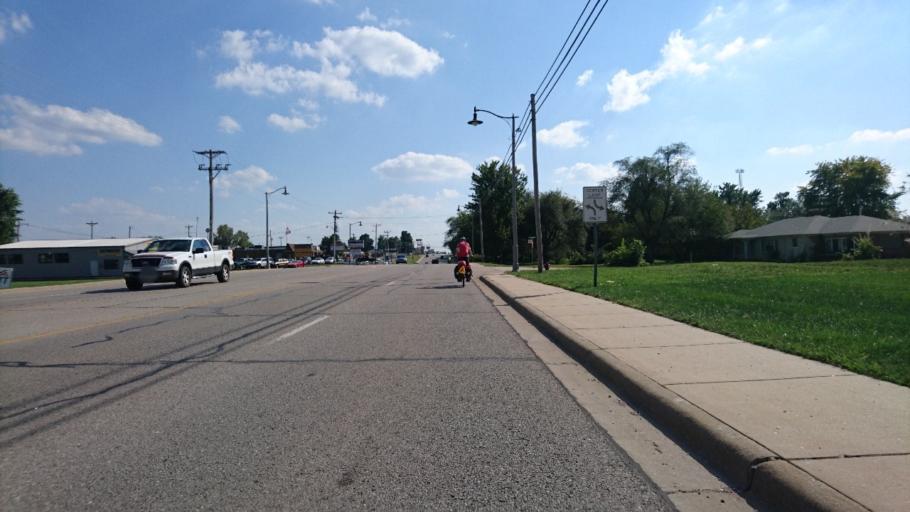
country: US
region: Missouri
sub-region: Laclede County
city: Lebanon
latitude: 37.6582
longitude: -92.6677
